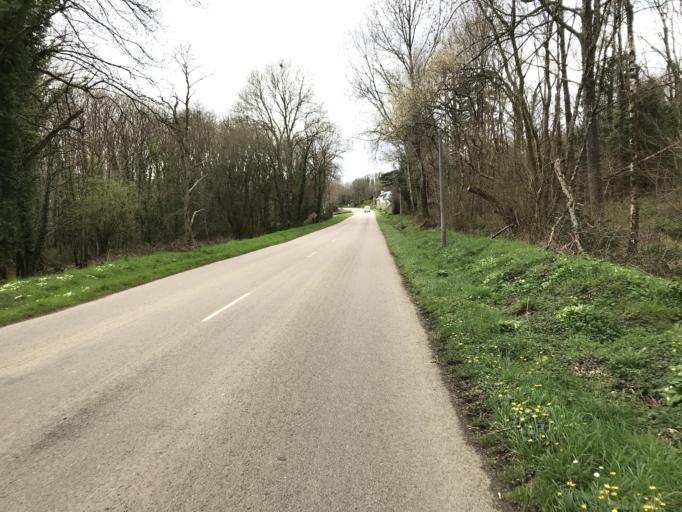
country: FR
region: Brittany
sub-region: Departement du Finistere
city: Hopital-Camfrout
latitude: 48.3139
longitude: -4.2170
